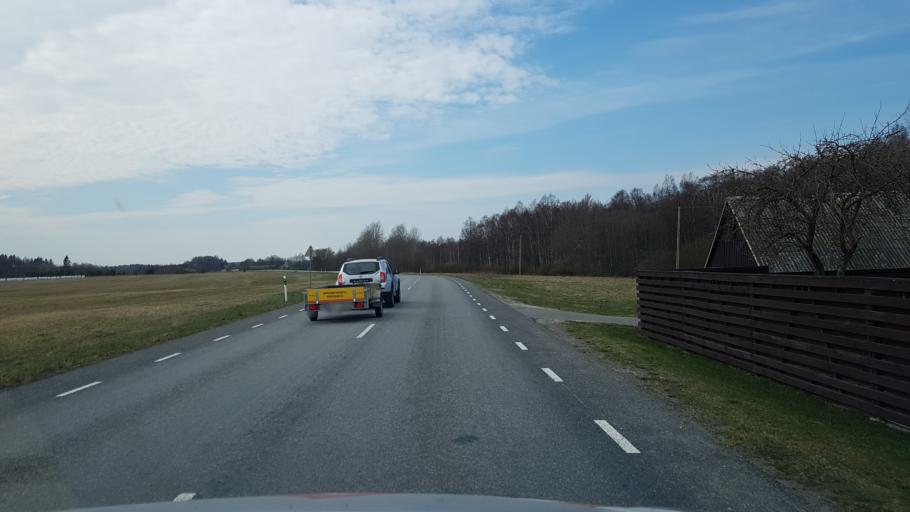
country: EE
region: Laeaene-Virumaa
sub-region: Haljala vald
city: Haljala
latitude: 59.4575
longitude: 26.2268
